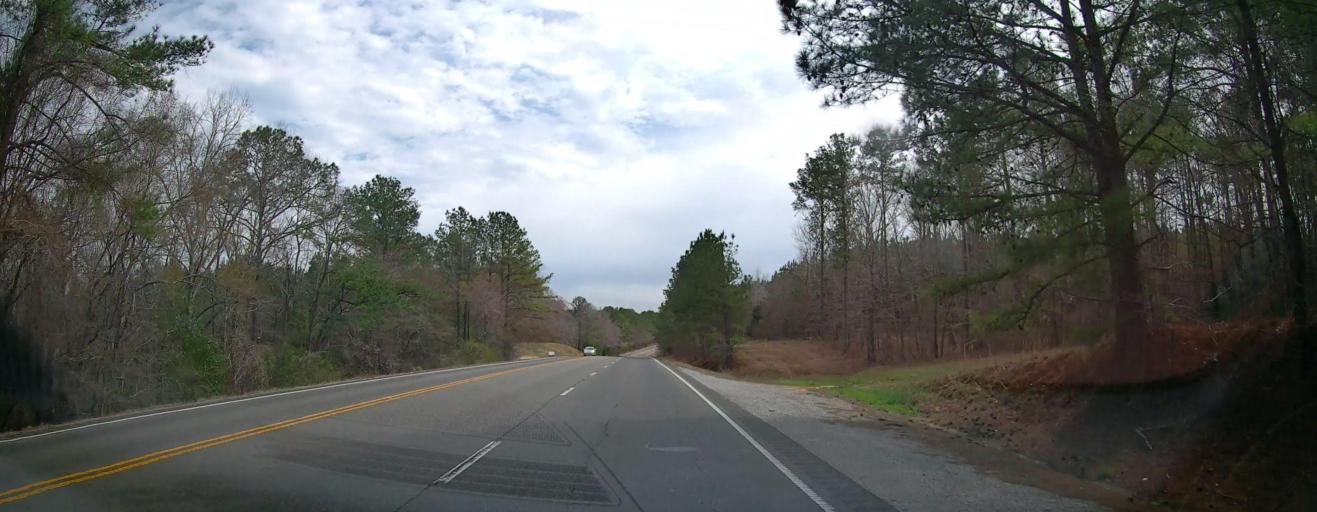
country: US
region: Alabama
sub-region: Marion County
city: Hamilton
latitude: 34.0635
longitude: -87.9703
